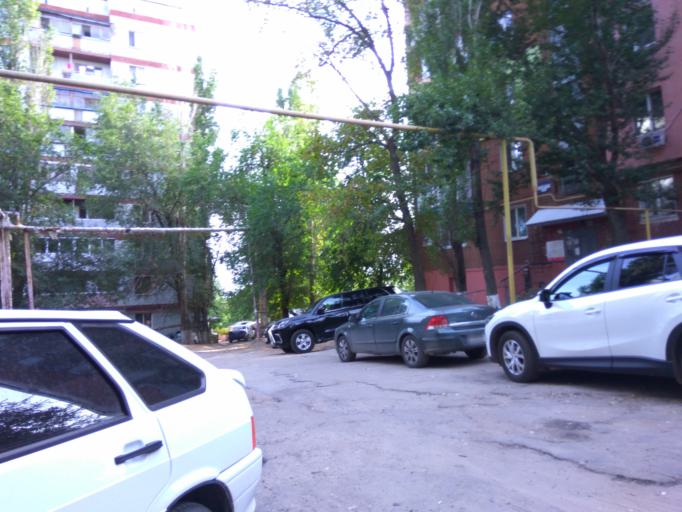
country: RU
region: Saratov
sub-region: Saratovskiy Rayon
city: Saratov
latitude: 51.5511
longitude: 46.0534
